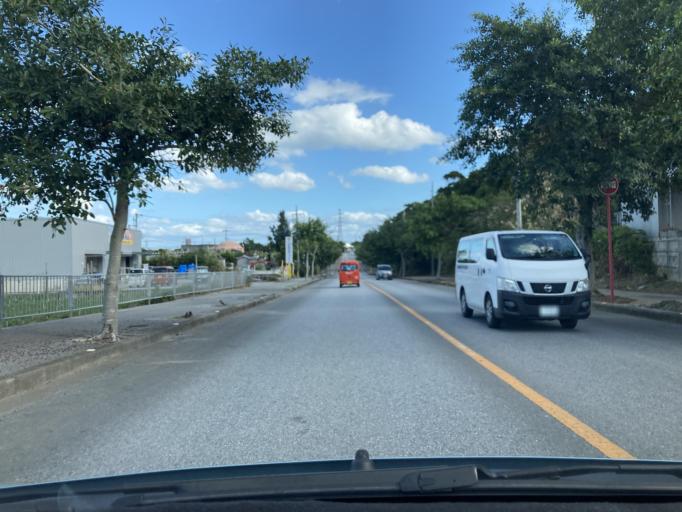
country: JP
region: Okinawa
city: Gushikawa
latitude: 26.3686
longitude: 127.8352
